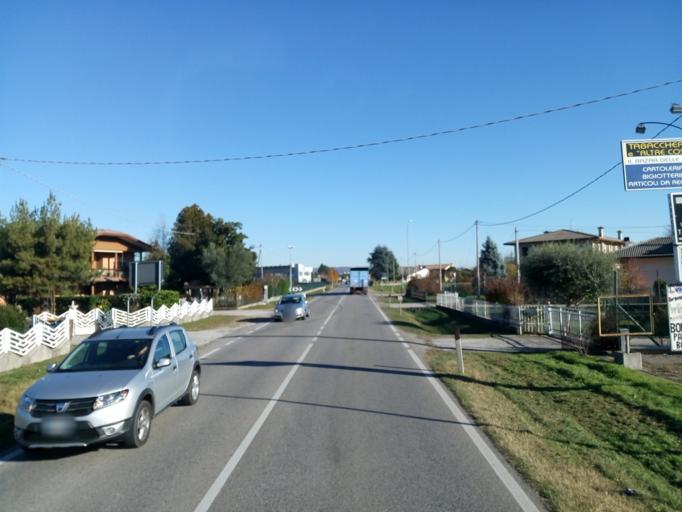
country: IT
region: Veneto
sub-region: Provincia di Treviso
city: Caselle
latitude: 45.7488
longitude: 11.9803
